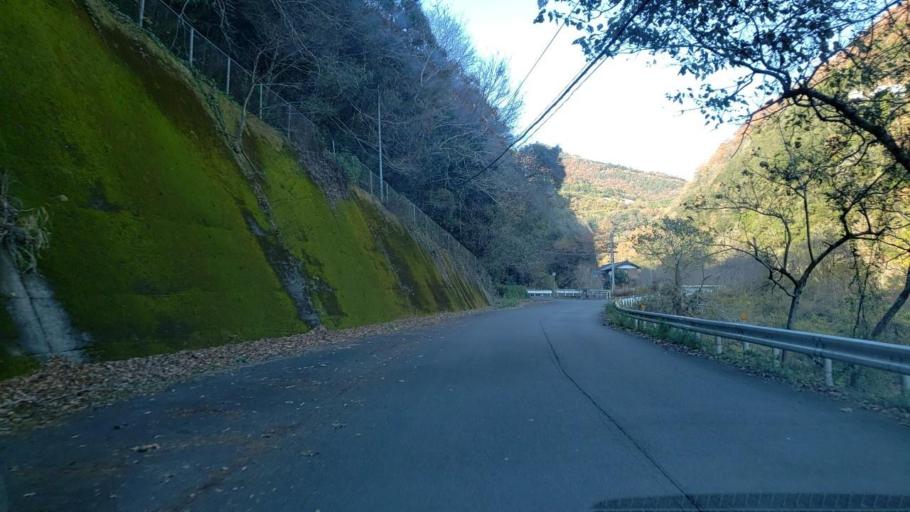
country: JP
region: Tokushima
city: Wakimachi
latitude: 34.0913
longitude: 134.0680
